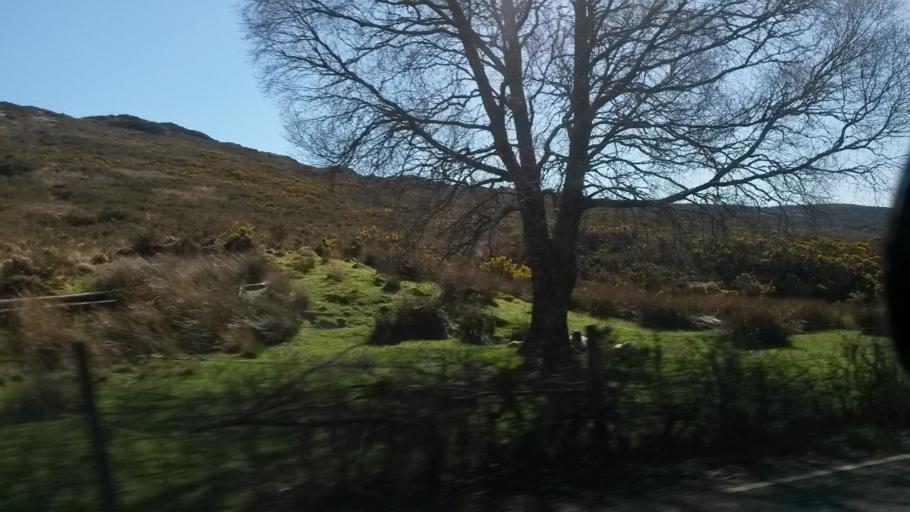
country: IE
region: Munster
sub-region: Ciarrai
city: Cill Airne
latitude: 51.9477
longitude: -9.3885
